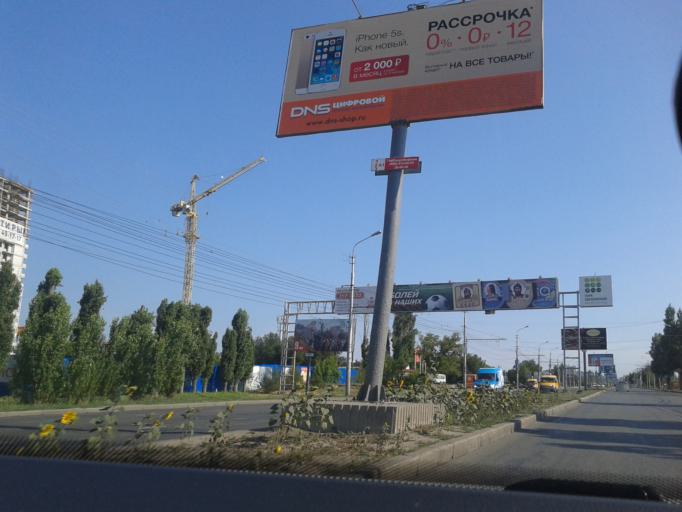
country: RU
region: Volgograd
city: Volgograd
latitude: 48.6245
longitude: 44.4260
